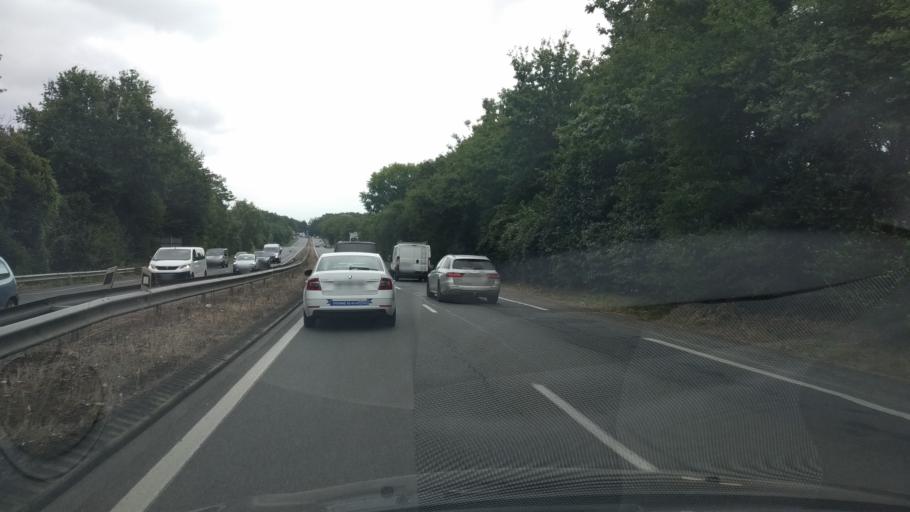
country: FR
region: Poitou-Charentes
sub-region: Departement de la Vienne
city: Biard
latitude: 46.5530
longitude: 0.3104
